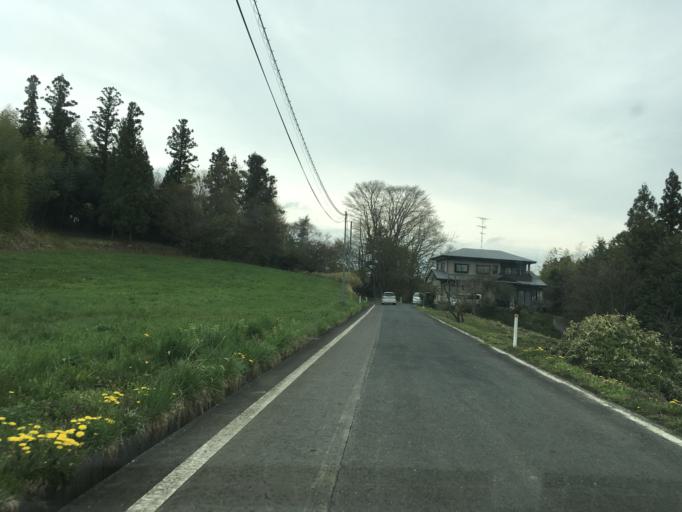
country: JP
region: Iwate
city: Ichinoseki
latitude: 38.8452
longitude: 141.3334
